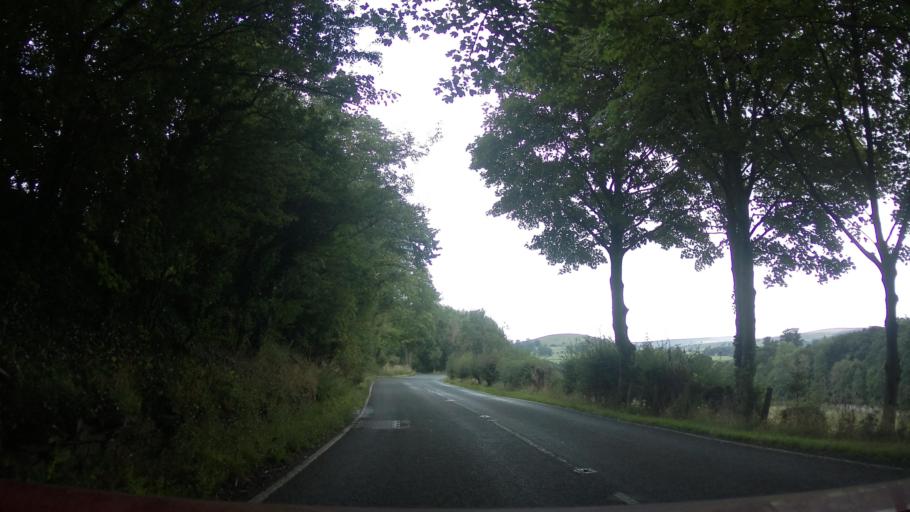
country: GB
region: England
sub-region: North Yorkshire
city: Leyburn
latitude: 54.3947
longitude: -1.8278
